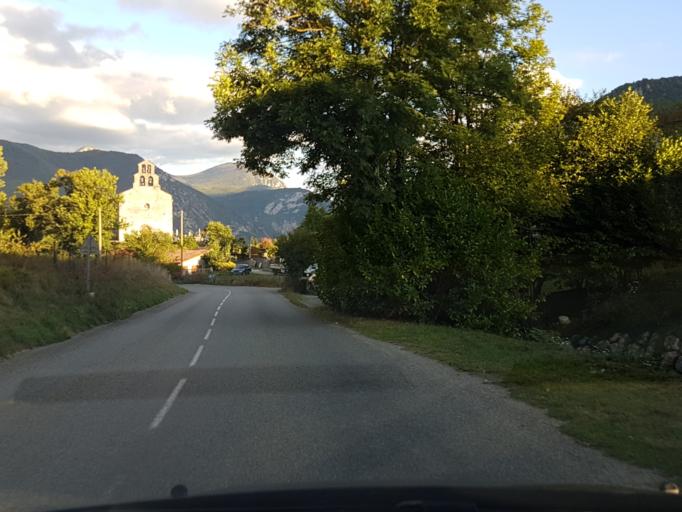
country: FR
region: Midi-Pyrenees
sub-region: Departement de l'Ariege
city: Tarascon-sur-Ariege
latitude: 42.8590
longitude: 1.5765
